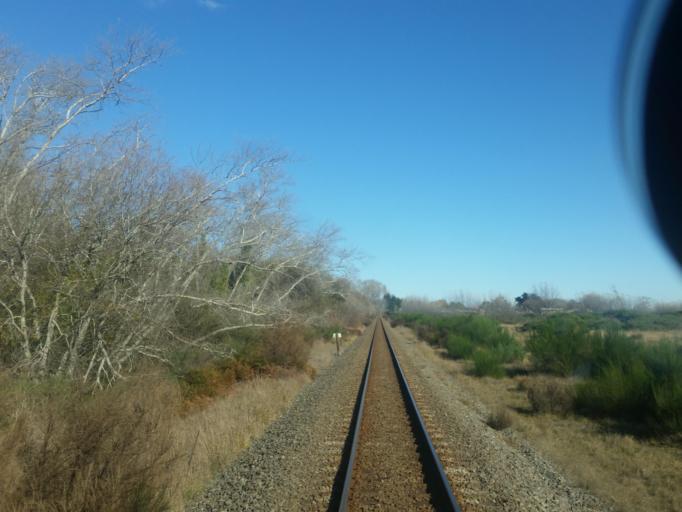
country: NZ
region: Canterbury
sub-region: Waimakariri District
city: Kaiapoi
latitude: -43.4250
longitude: 172.6565
